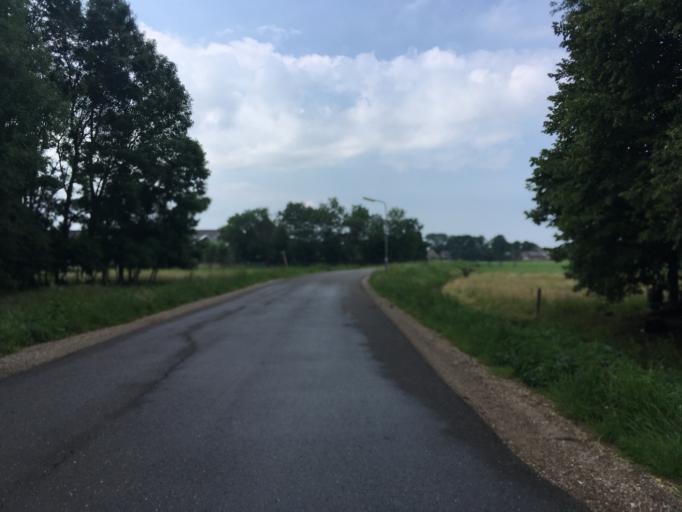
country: NL
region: North Holland
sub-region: Gemeente Haarlem
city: Haarlem
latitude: 52.4060
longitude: 4.7005
